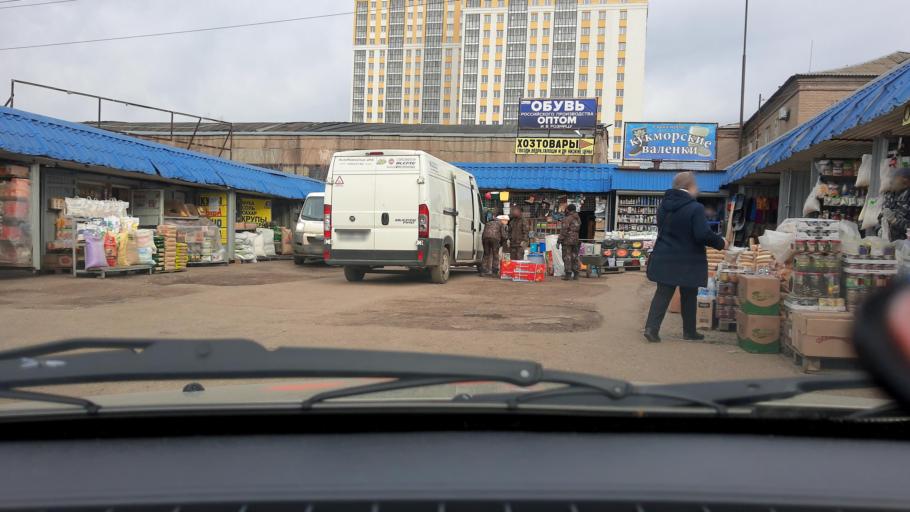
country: RU
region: Bashkortostan
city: Ufa
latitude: 54.7137
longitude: 55.9877
